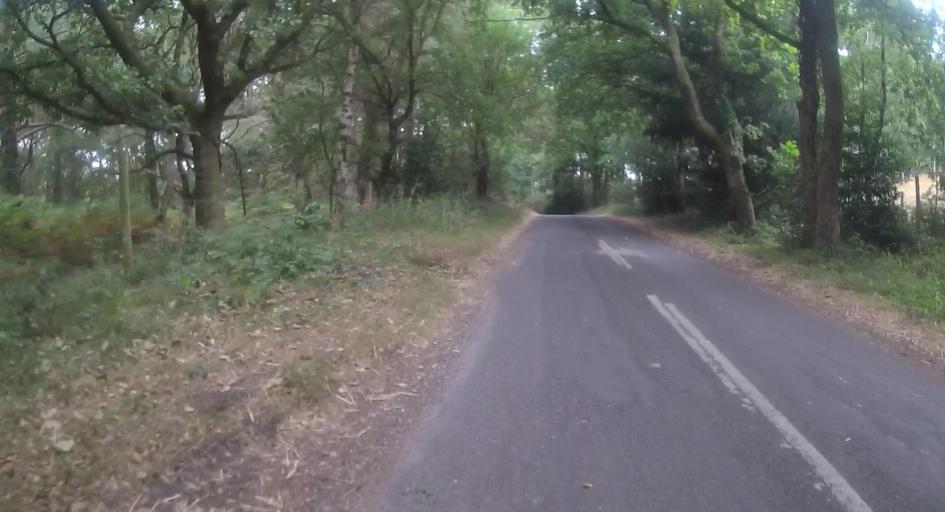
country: GB
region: England
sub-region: Dorset
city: Bovington Camp
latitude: 50.7310
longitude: -2.2491
